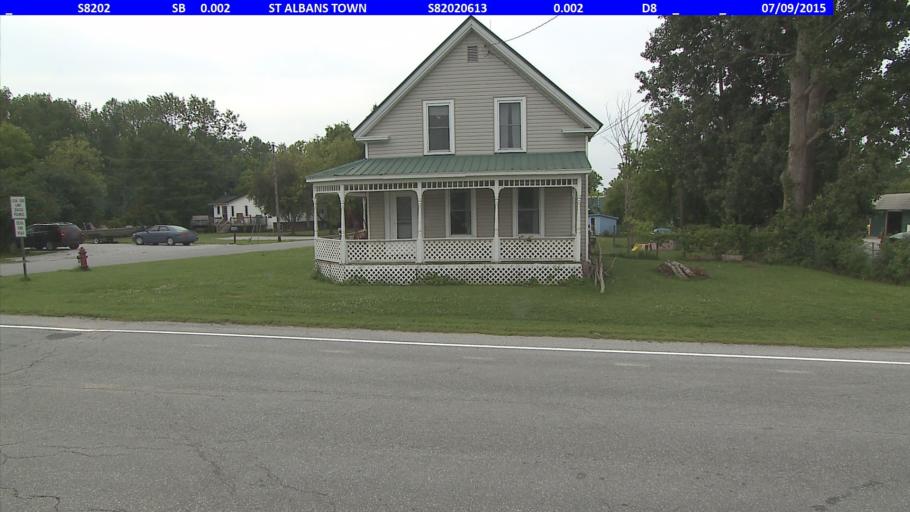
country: US
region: Vermont
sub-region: Franklin County
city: Saint Albans
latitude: 44.8120
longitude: -73.1072
